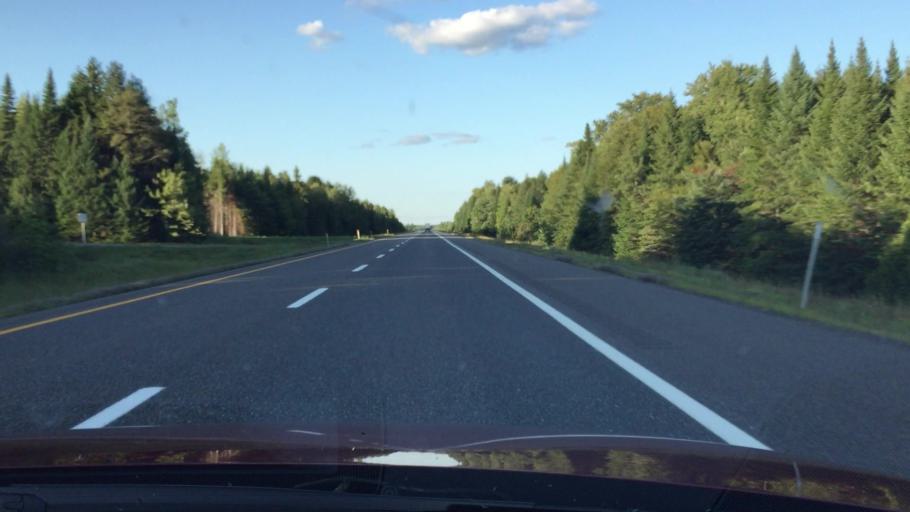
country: US
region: Maine
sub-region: Penobscot County
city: Patten
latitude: 46.0551
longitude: -68.2384
